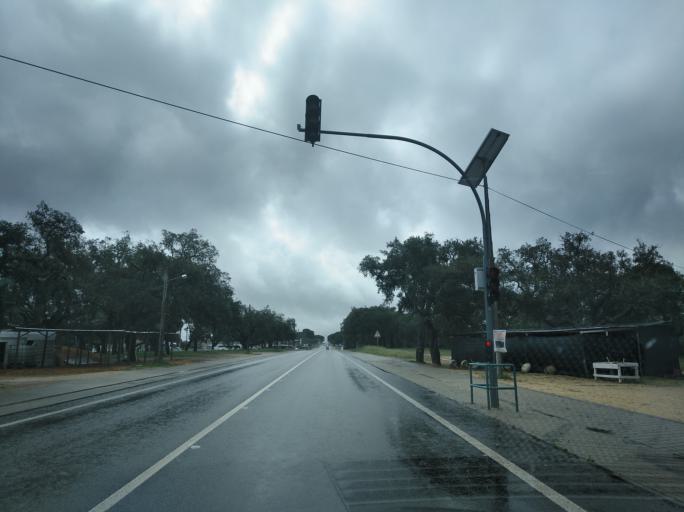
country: PT
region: Setubal
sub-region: Grandola
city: Grandola
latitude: 38.2301
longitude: -8.5544
